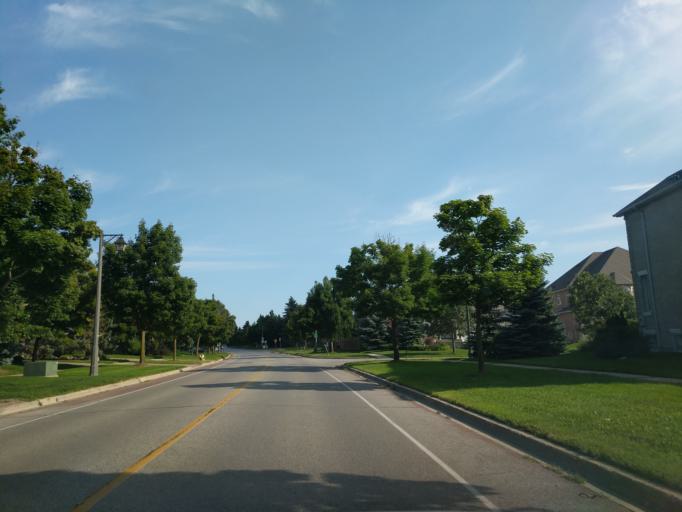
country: CA
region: Ontario
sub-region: York
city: Richmond Hill
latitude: 43.8649
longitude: -79.3998
